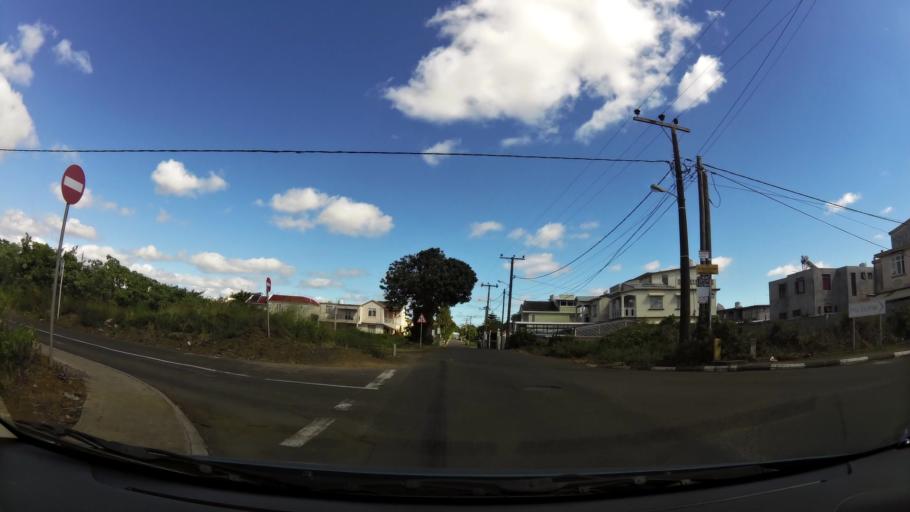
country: MU
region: Plaines Wilhems
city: Vacoas
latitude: -20.2880
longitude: 57.4777
